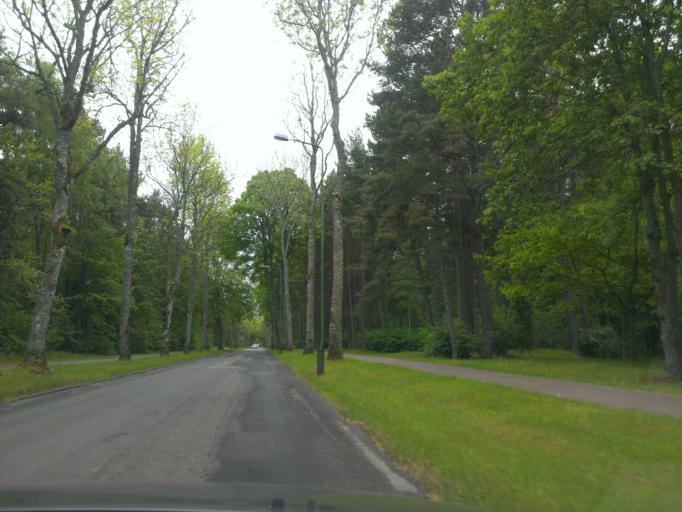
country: LT
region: Klaipedos apskritis
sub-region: Klaipeda
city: Palanga
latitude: 55.9017
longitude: 21.0618
